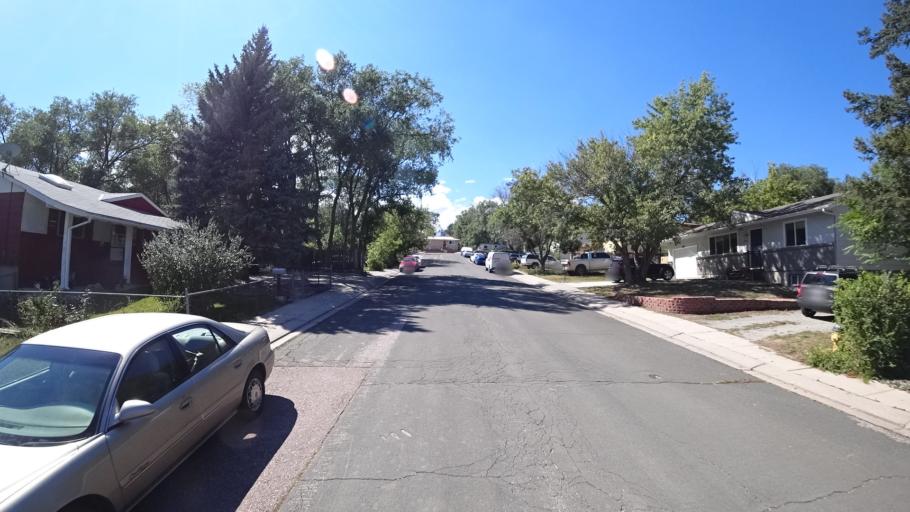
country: US
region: Colorado
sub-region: El Paso County
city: Colorado Springs
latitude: 38.8564
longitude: -104.8572
